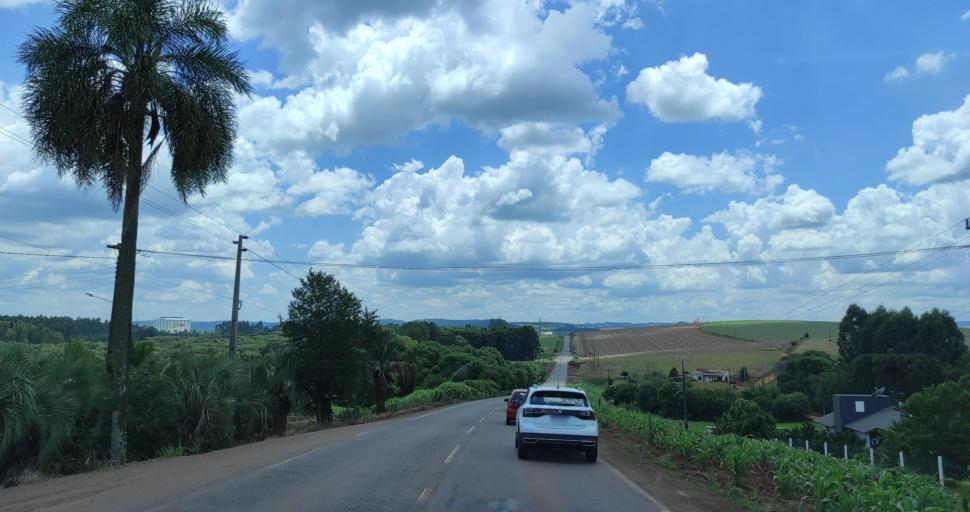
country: BR
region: Santa Catarina
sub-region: Xanxere
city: Xanxere
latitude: -26.7744
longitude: -52.4066
